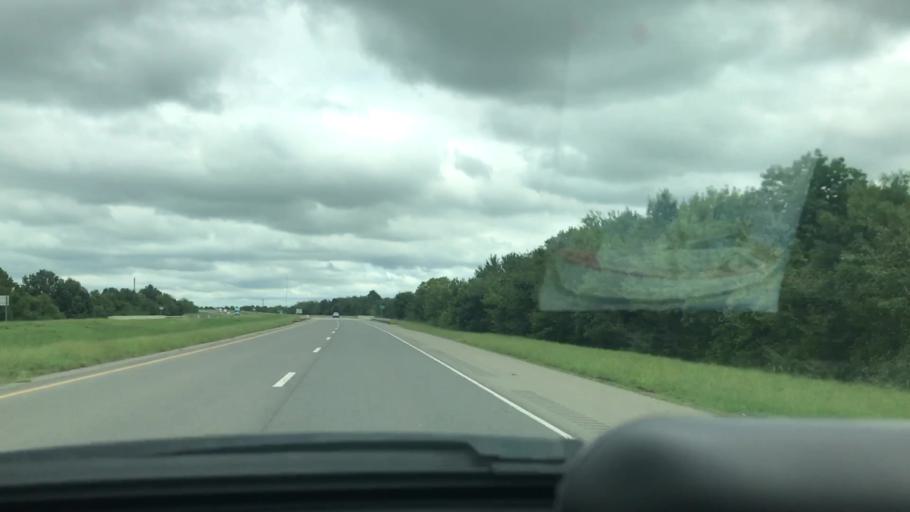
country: US
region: Oklahoma
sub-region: McIntosh County
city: Checotah
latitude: 35.5618
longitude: -95.4932
